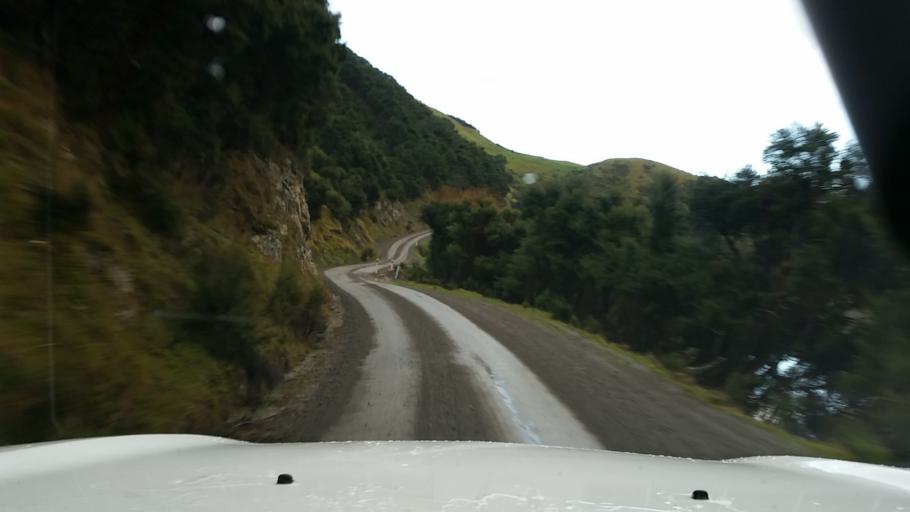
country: NZ
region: Wellington
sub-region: South Wairarapa District
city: Waipawa
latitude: -41.3731
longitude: 175.7154
